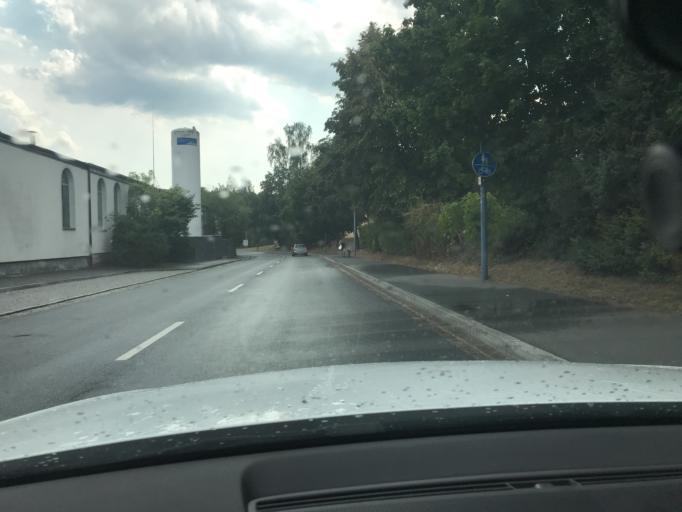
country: DE
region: Bavaria
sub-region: Upper Palatinate
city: Grafenwohr
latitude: 49.7267
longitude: 11.9024
